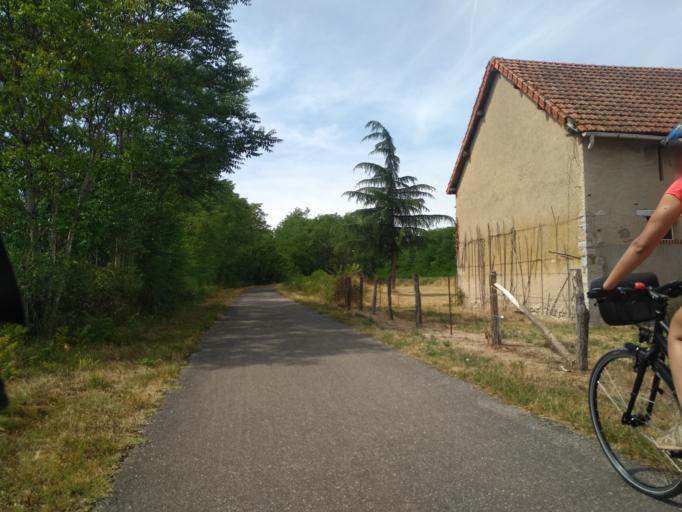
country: FR
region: Auvergne
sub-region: Departement de l'Allier
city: Diou
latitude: 46.5420
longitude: 3.7479
